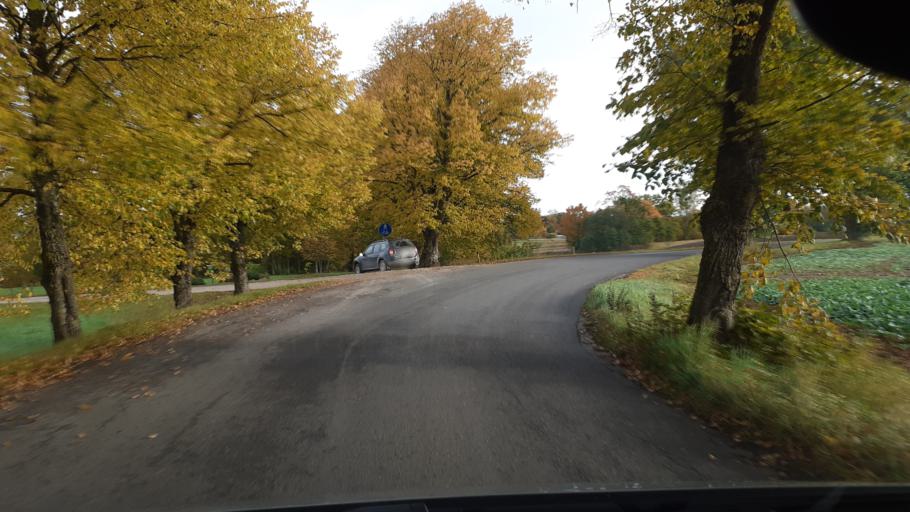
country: LV
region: Kuldigas Rajons
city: Kuldiga
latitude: 57.0134
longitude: 21.9039
